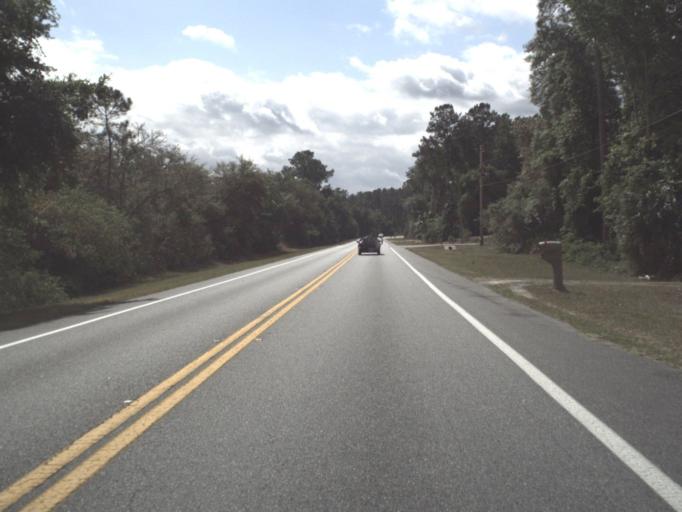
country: US
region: Florida
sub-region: Marion County
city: Ocala
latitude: 29.2284
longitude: -82.0388
